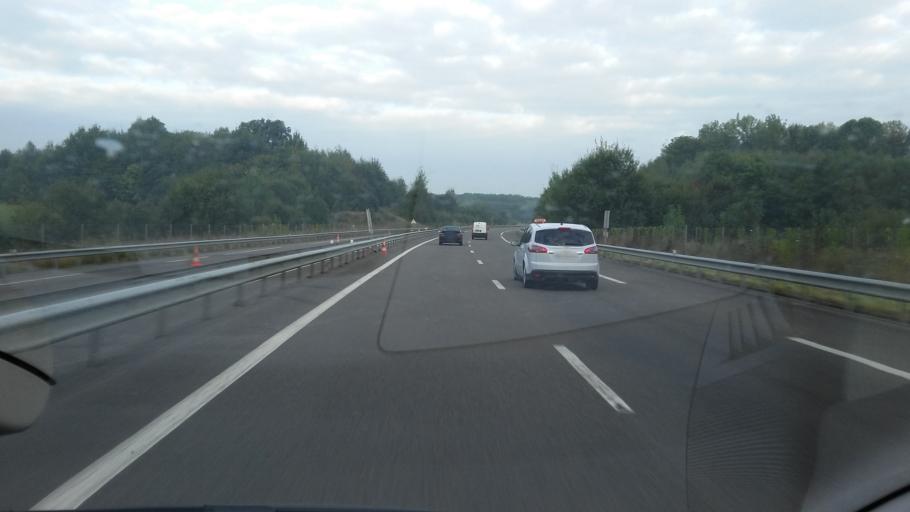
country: FR
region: Champagne-Ardenne
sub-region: Departement des Ardennes
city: La Francheville
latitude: 49.6393
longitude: 4.6087
